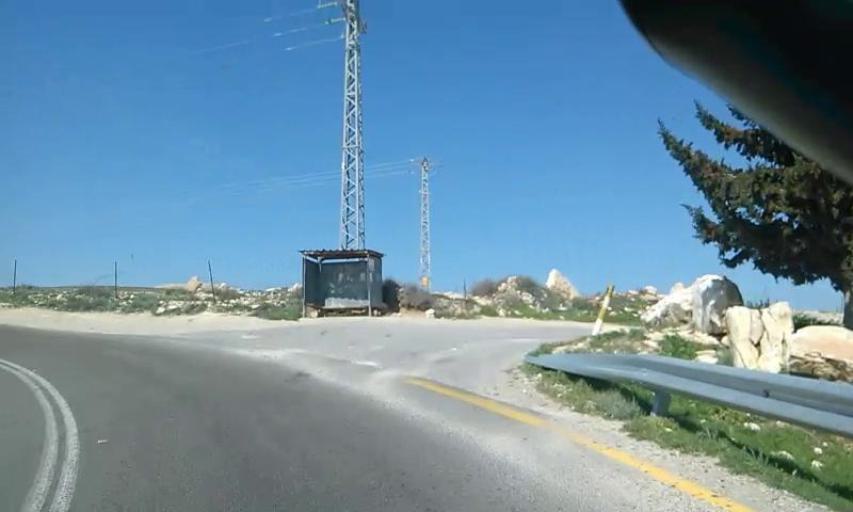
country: PS
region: West Bank
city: Jannatah
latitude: 31.6517
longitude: 35.2059
